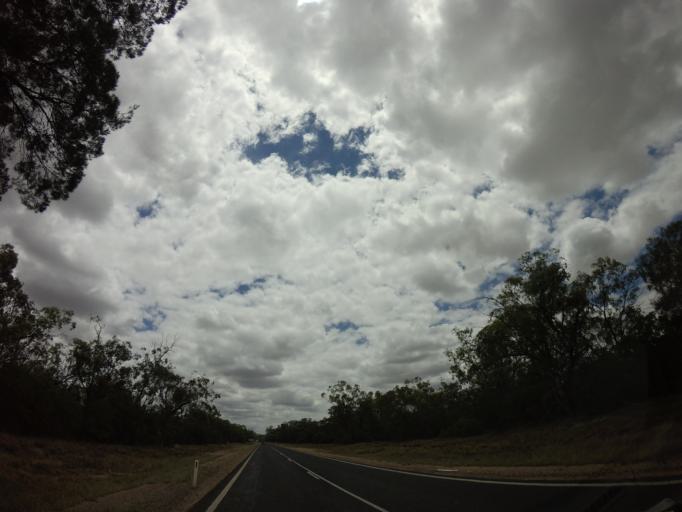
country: AU
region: Queensland
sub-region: Goondiwindi
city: Goondiwindi
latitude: -28.4633
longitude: 150.2948
